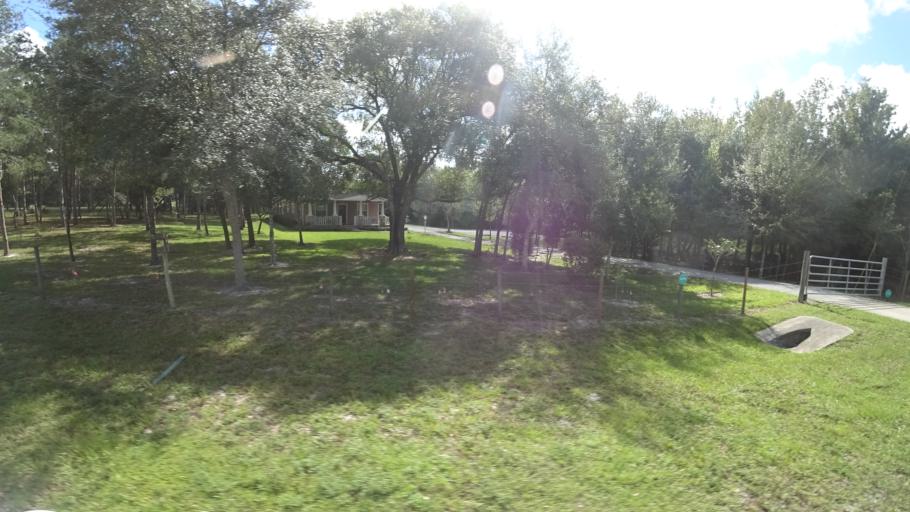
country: US
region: Florida
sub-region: Sarasota County
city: Lake Sarasota
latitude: 27.3575
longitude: -82.2294
